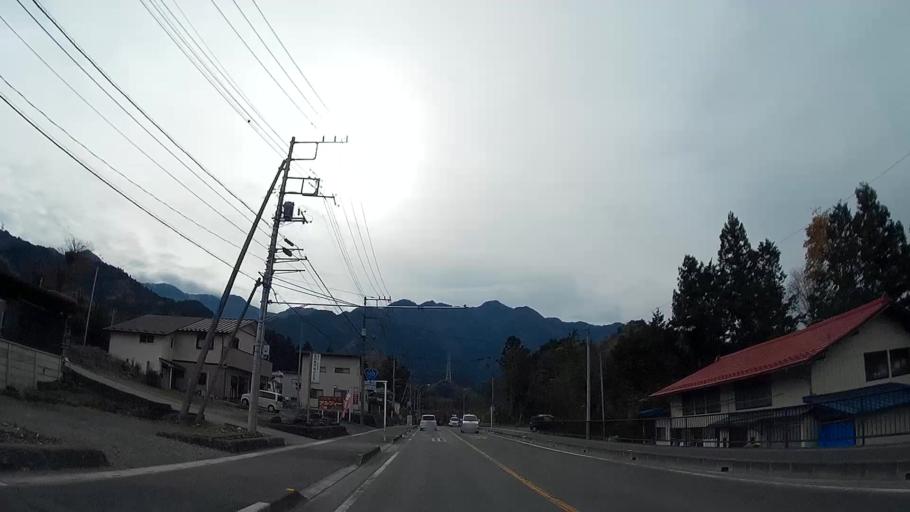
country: JP
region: Saitama
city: Chichibu
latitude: 35.9550
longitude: 139.0285
